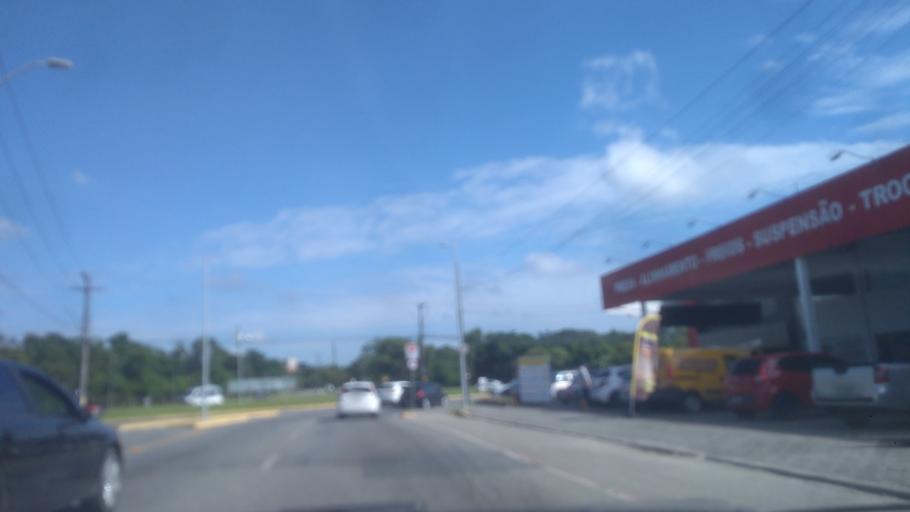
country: BR
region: Santa Catarina
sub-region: Joinville
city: Joinville
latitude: -26.3174
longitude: -48.8284
